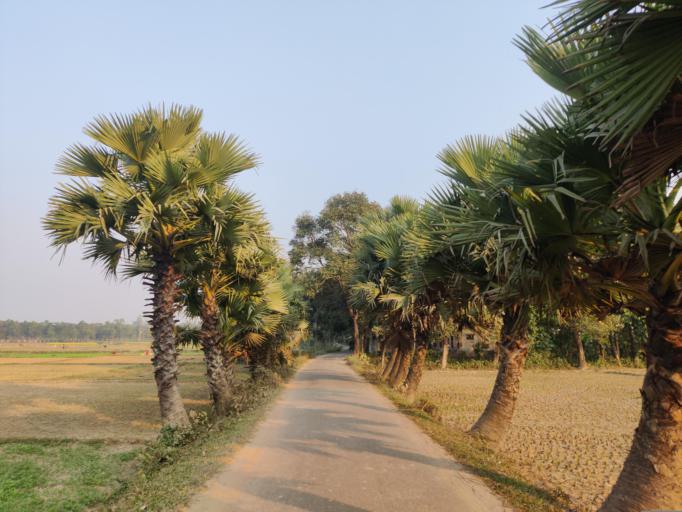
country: BD
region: Dhaka
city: Narsingdi
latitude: 24.0947
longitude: 90.7088
